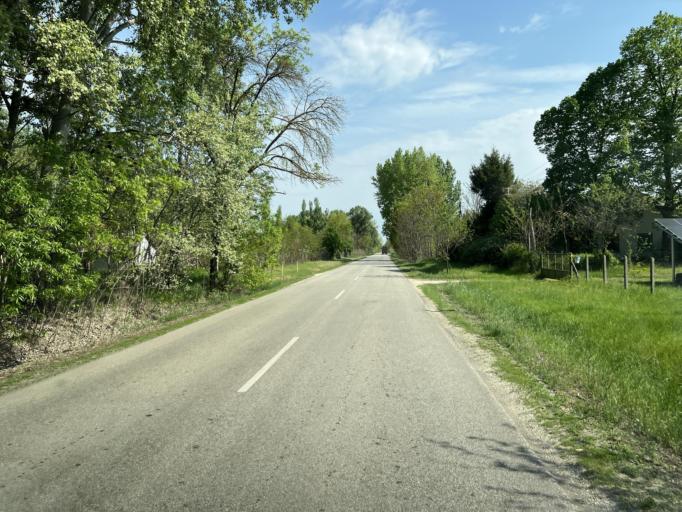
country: HU
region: Pest
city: Kocser
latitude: 47.0248
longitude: 19.9353
